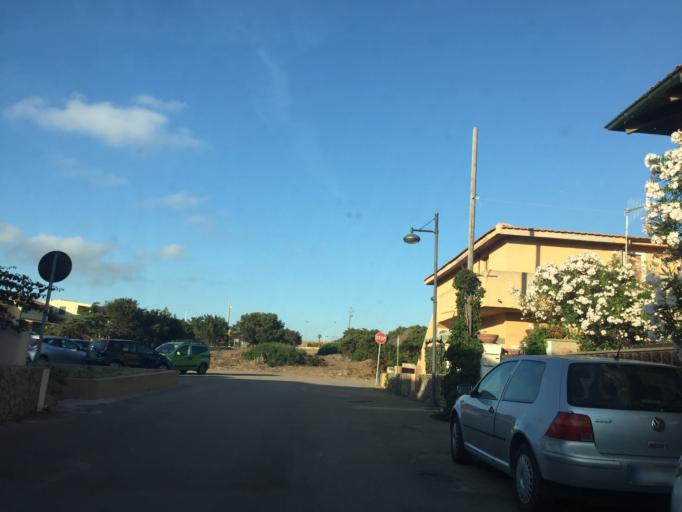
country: IT
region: Sardinia
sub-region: Provincia di Olbia-Tempio
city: Trinita d'Agultu
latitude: 41.0116
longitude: 8.8788
